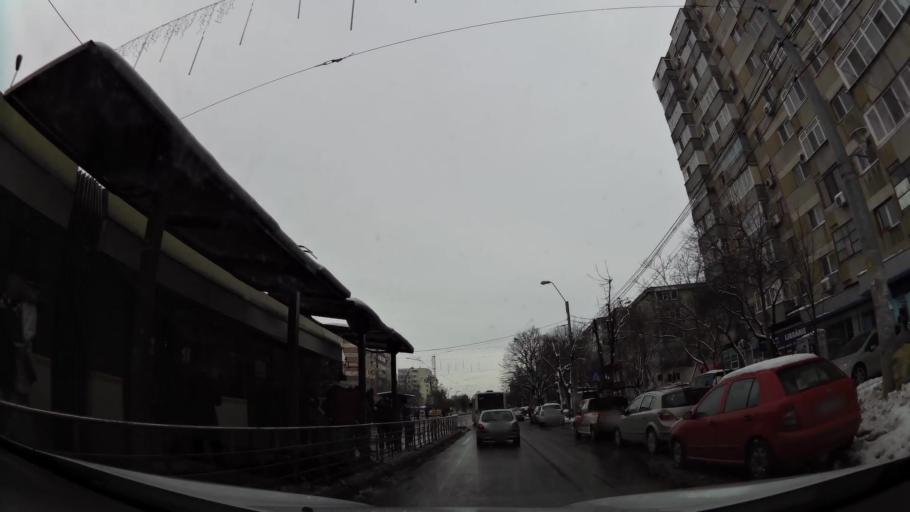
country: RO
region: Ilfov
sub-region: Comuna Popesti-Leordeni
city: Popesti-Leordeni
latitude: 44.3891
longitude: 26.1322
